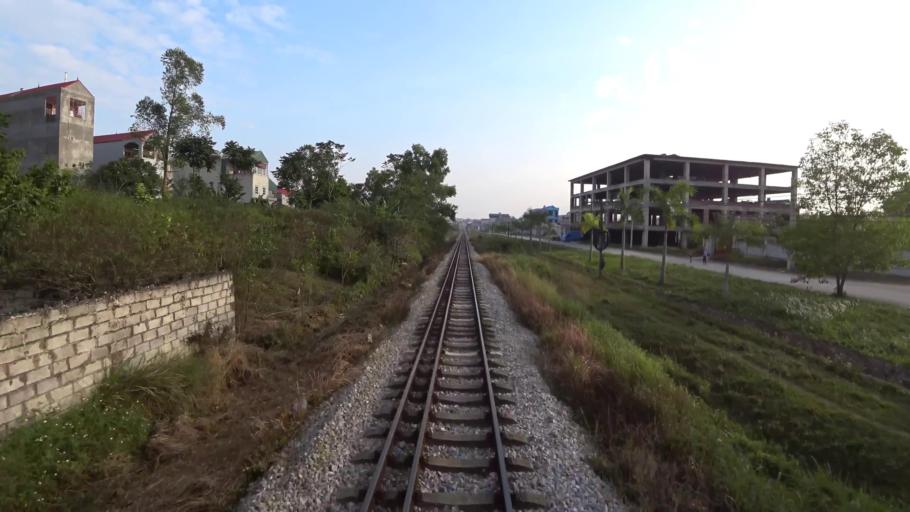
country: VN
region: Lang Son
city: Thi Tran Cao Loc
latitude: 21.8819
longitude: 106.7489
